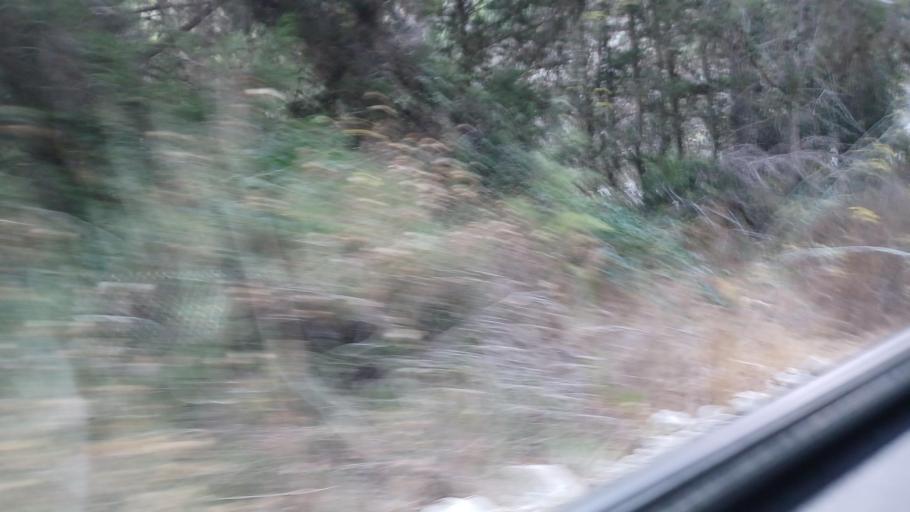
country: CY
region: Pafos
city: Tala
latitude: 34.8664
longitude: 32.4619
